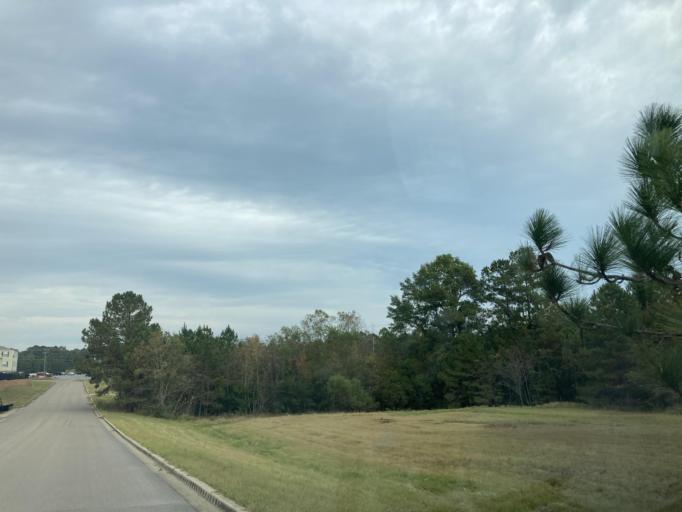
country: US
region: Mississippi
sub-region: Lamar County
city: West Hattiesburg
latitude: 31.3238
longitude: -89.4123
